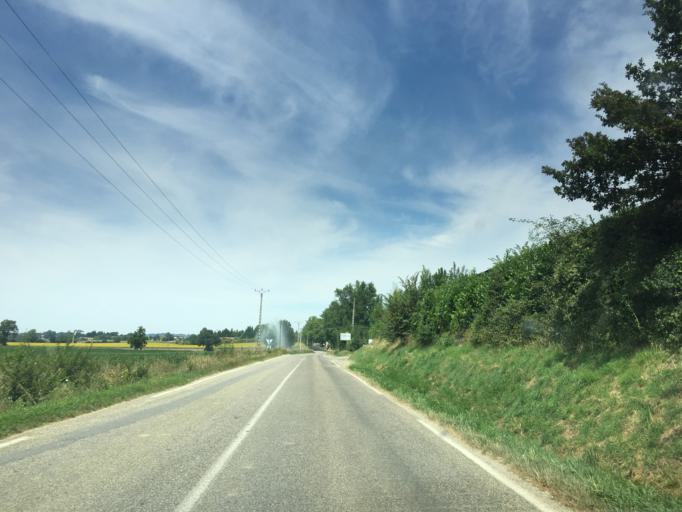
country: FR
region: Midi-Pyrenees
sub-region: Departement du Gers
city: Fleurance
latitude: 43.8493
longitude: 0.6769
